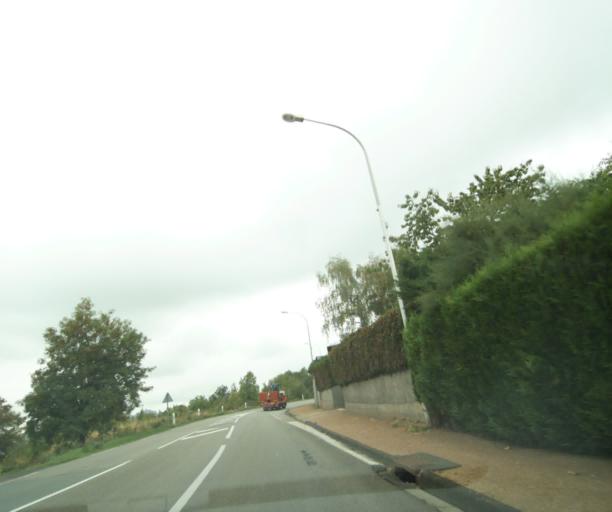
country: FR
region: Auvergne
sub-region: Departement du Puy-de-Dome
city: Royat
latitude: 45.7556
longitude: 3.0642
